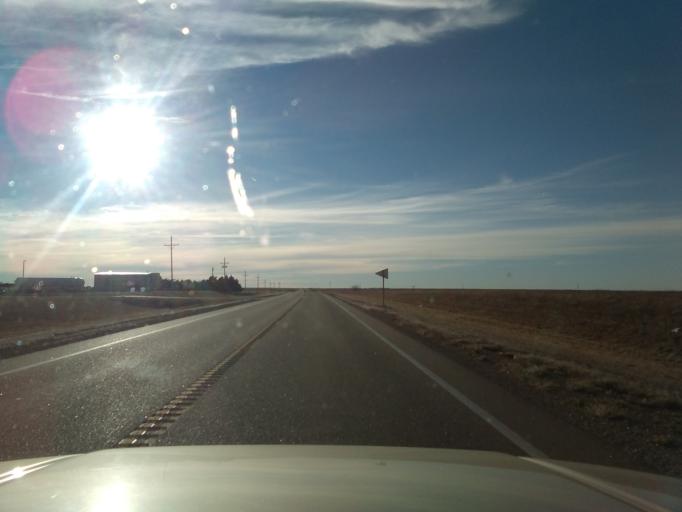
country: US
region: Kansas
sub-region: Sheridan County
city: Hoxie
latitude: 39.5373
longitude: -100.5837
